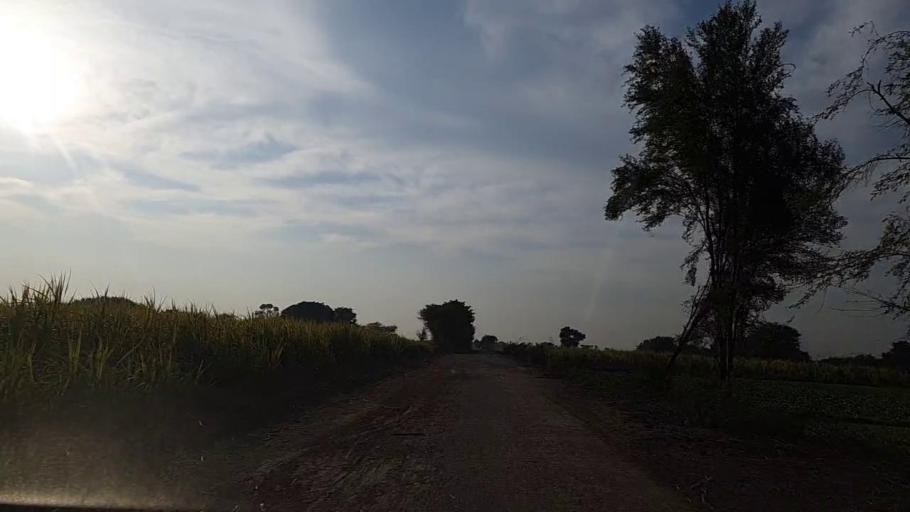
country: PK
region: Sindh
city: Bandhi
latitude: 26.5646
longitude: 68.2668
